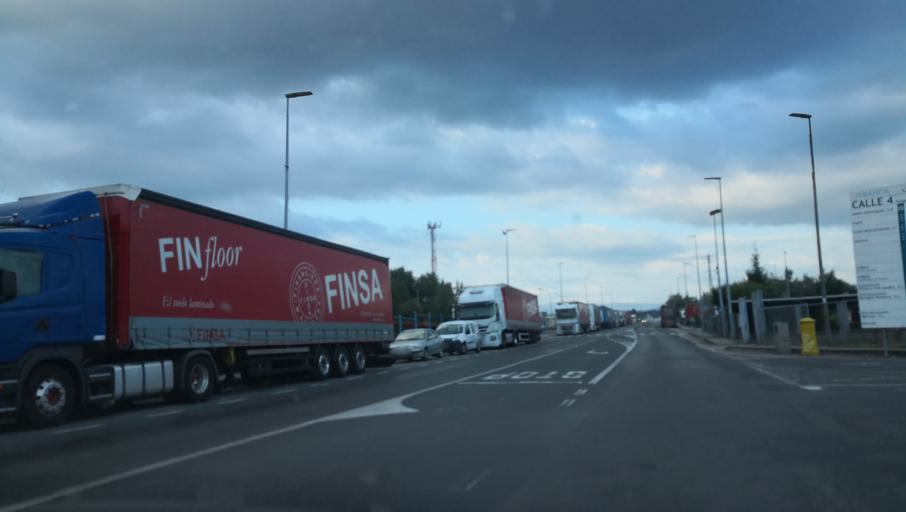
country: ES
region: Galicia
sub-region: Provincia de Ourense
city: Taboadela
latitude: 42.2892
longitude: -7.8212
